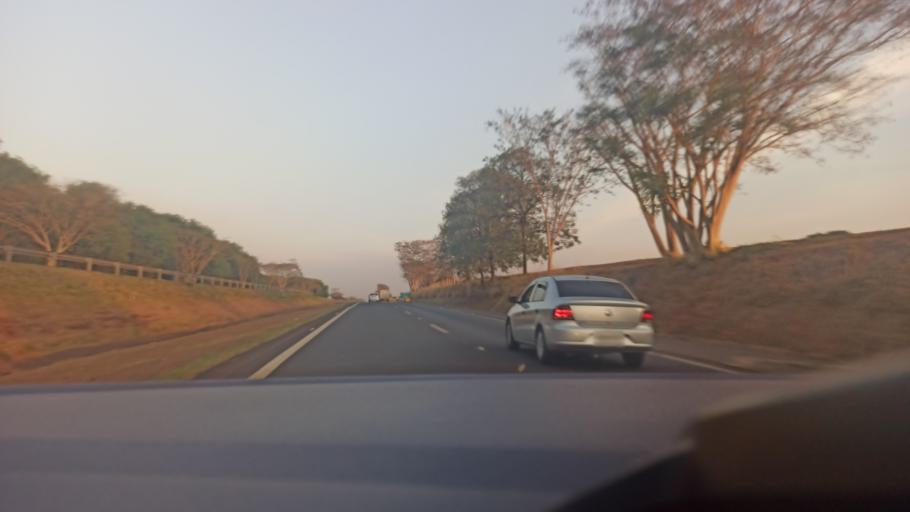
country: BR
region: Sao Paulo
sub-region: Taquaritinga
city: Taquaritinga
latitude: -21.4540
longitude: -48.6300
